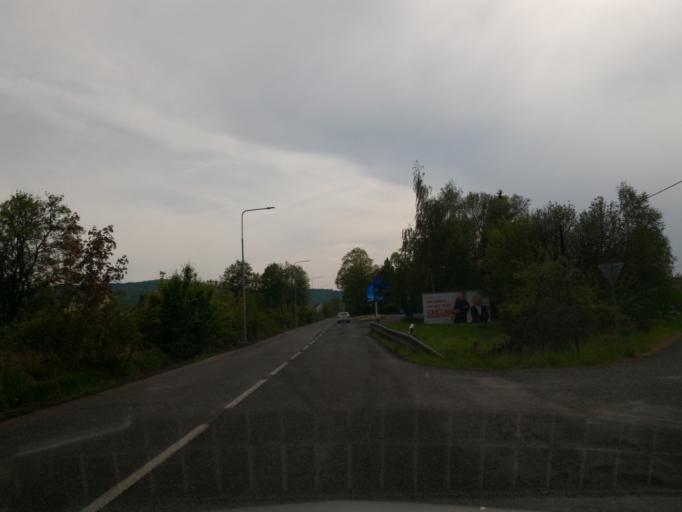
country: CZ
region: Ustecky
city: Varnsdorf
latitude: 50.8970
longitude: 14.6273
